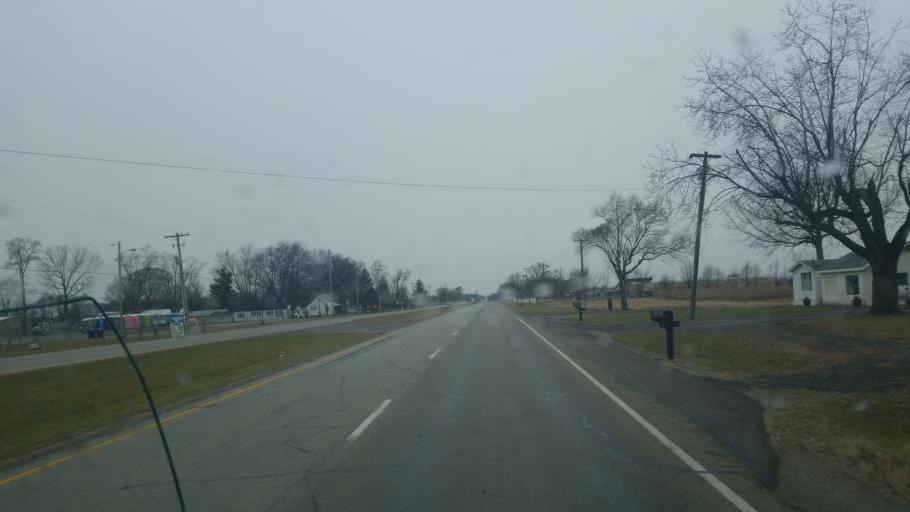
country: US
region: Indiana
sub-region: Hancock County
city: Greenfield
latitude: 39.7875
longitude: -85.7214
